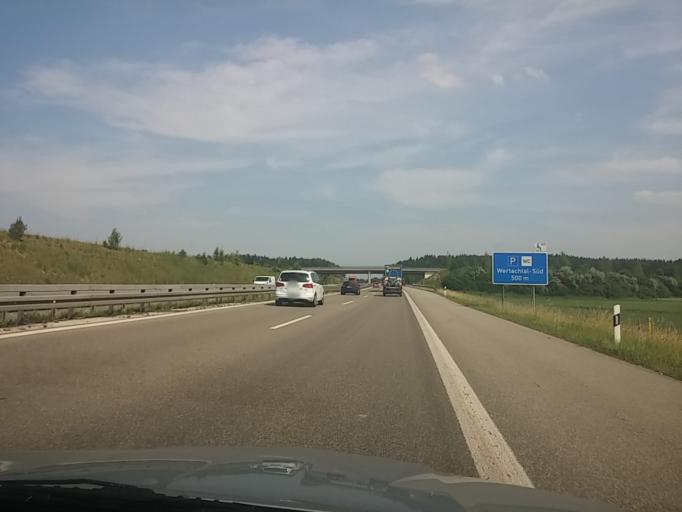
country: DE
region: Bavaria
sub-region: Swabia
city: Wiedergeltingen
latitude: 48.0322
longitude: 10.6598
